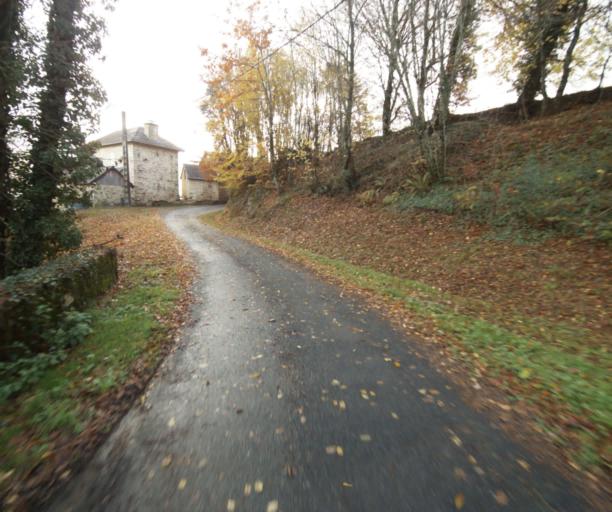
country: FR
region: Limousin
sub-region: Departement de la Correze
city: Cornil
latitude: 45.2241
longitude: 1.6656
